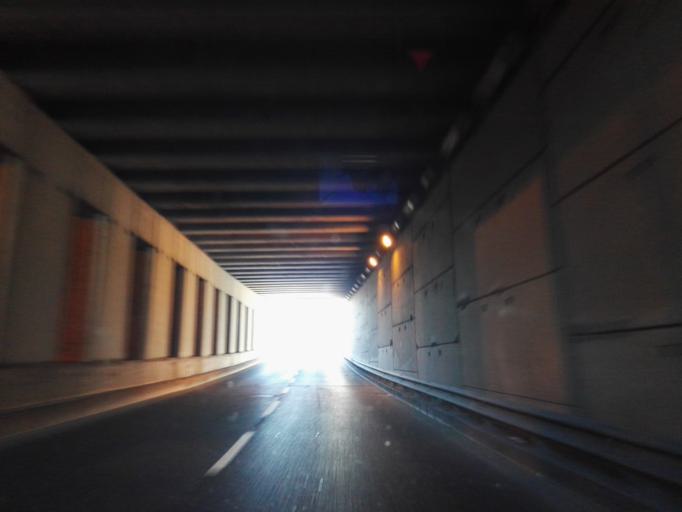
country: PT
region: Lisbon
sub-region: Loures
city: Moscavide
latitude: 38.7758
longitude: -9.1103
